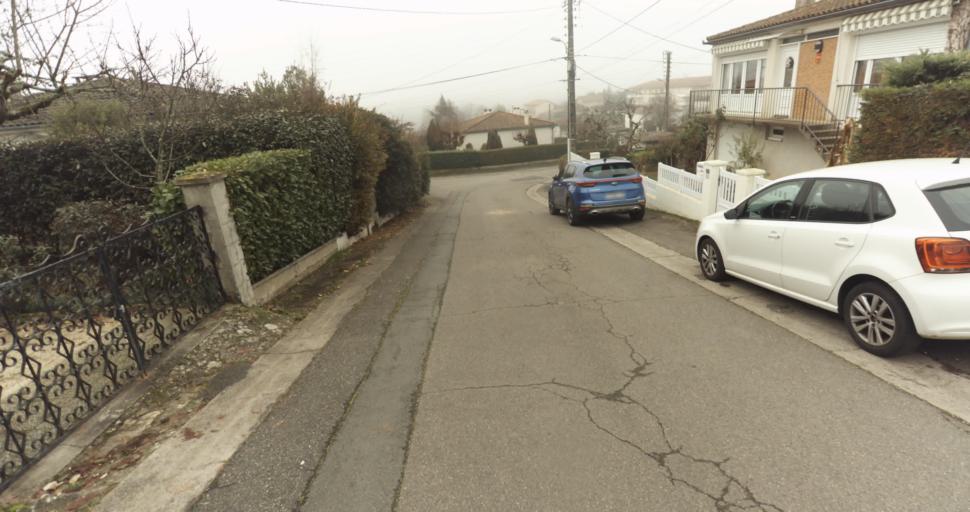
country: FR
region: Midi-Pyrenees
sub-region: Departement du Lot
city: Figeac
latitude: 44.6182
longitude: 2.0422
